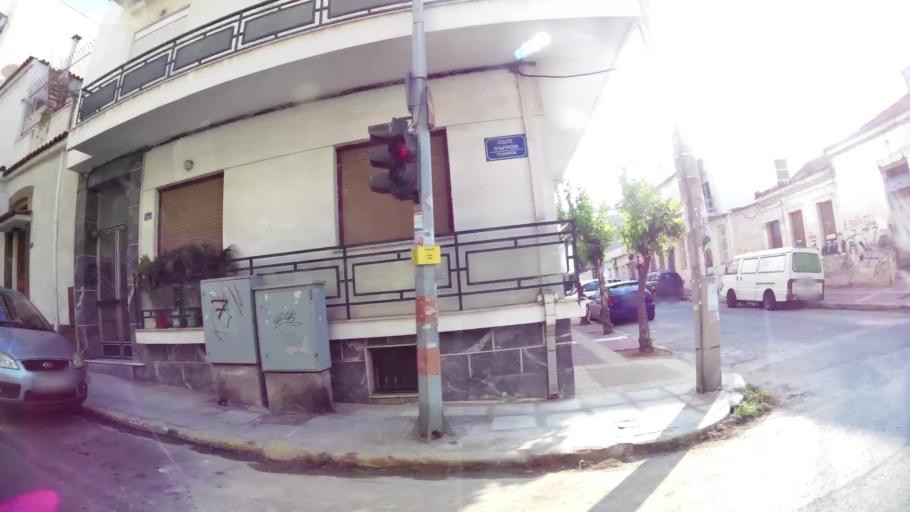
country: GR
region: Attica
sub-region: Nomos Attikis
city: Piraeus
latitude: 37.9609
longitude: 23.6337
